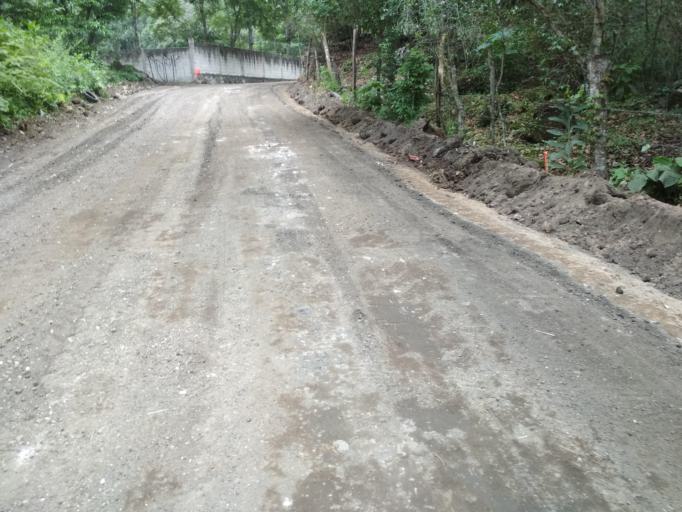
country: MX
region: Veracruz
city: Jilotepec
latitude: 19.6174
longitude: -96.9307
